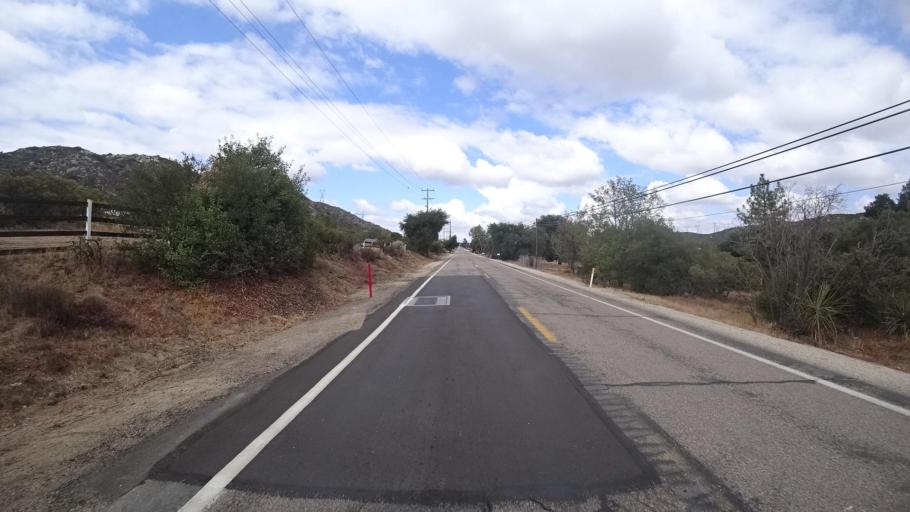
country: US
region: California
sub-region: San Diego County
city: Campo
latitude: 32.6504
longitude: -116.4874
